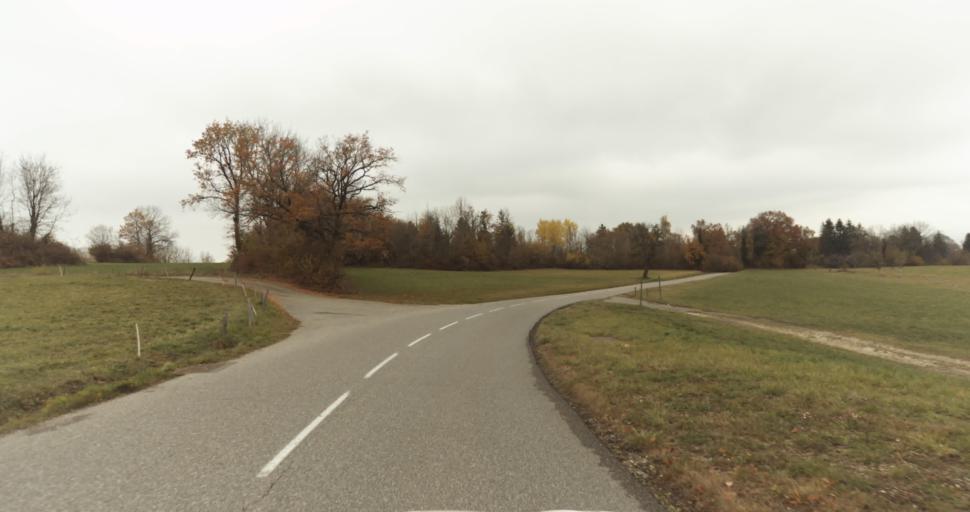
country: FR
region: Rhone-Alpes
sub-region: Departement de la Haute-Savoie
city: Seynod
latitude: 45.8518
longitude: 6.0843
